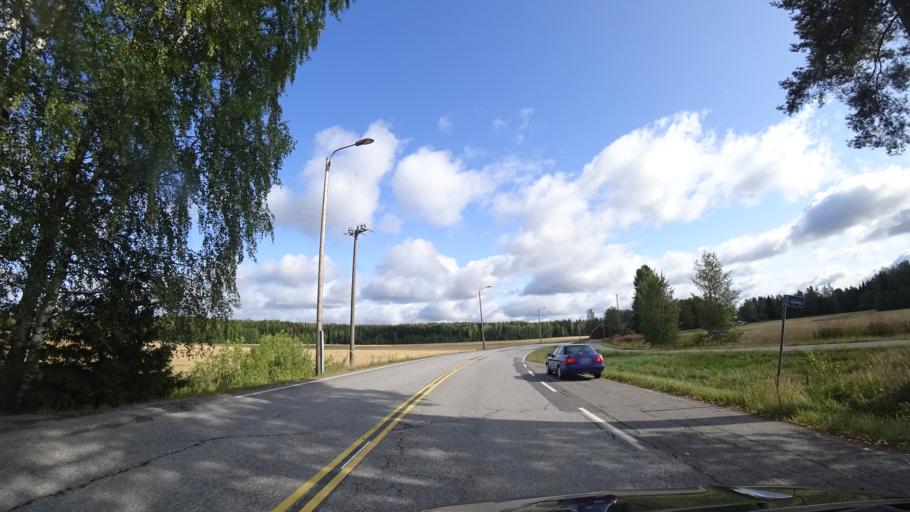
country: FI
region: Uusimaa
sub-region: Helsinki
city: Hyvinge
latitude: 60.5755
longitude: 24.9812
